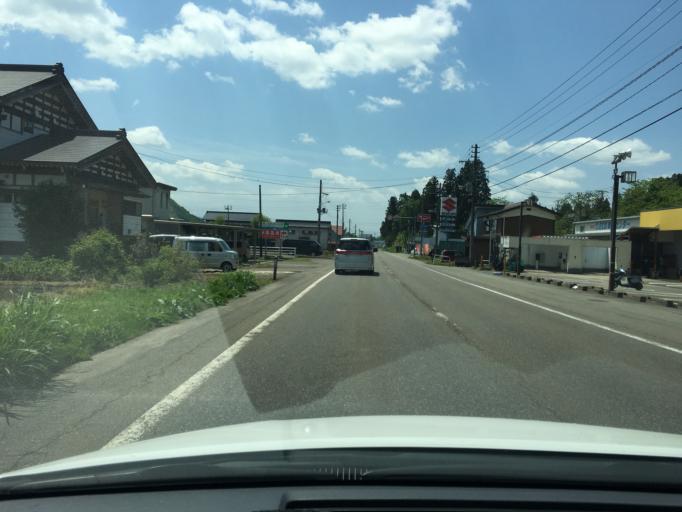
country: JP
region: Niigata
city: Ojiya
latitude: 37.2849
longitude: 138.9869
